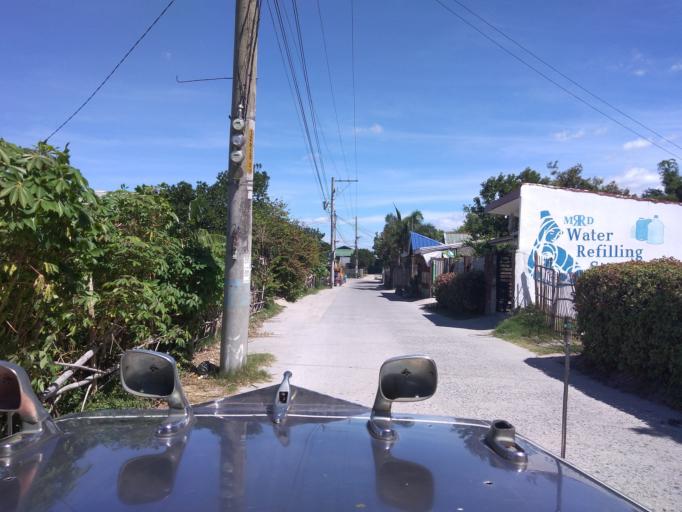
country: PH
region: Central Luzon
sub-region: Province of Pampanga
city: Magliman
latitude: 15.0313
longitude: 120.6491
